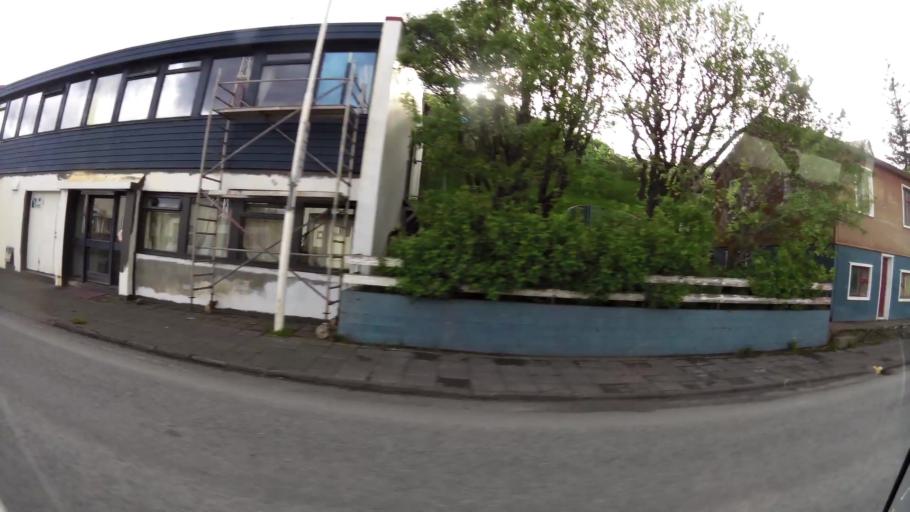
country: IS
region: West
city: Borgarnes
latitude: 64.5383
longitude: -21.9213
